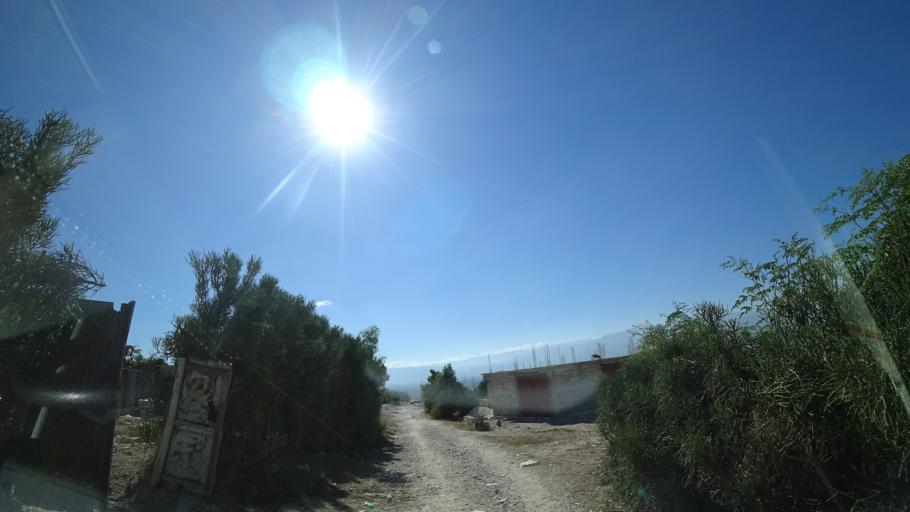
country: HT
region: Ouest
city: Croix des Bouquets
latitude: 18.6751
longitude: -72.2399
